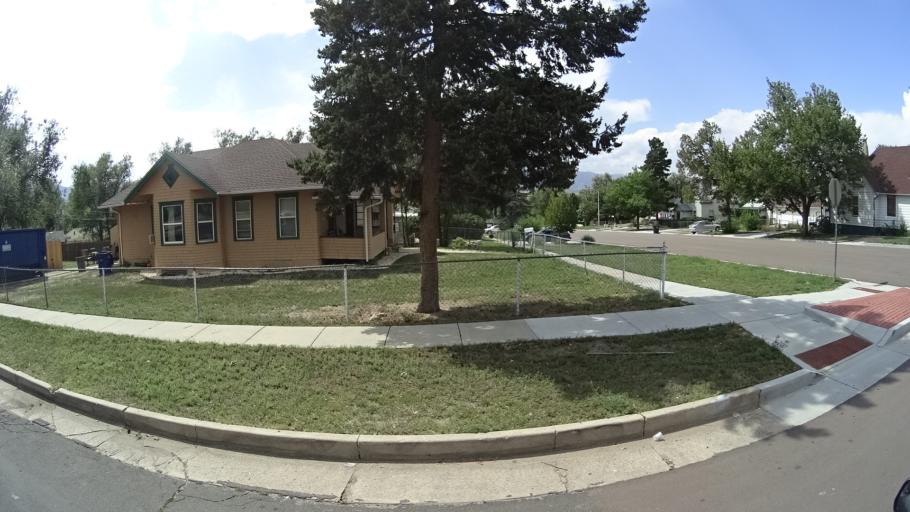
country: US
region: Colorado
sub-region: El Paso County
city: Colorado Springs
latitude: 38.8249
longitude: -104.8108
